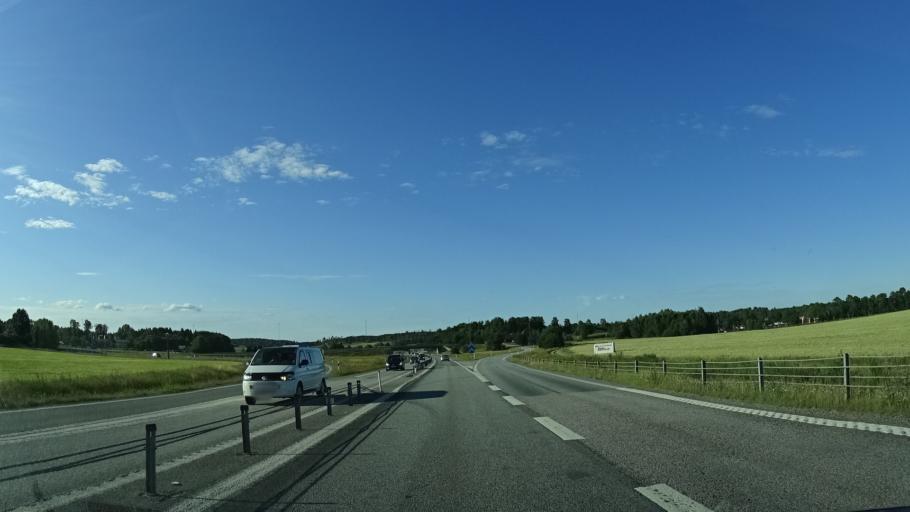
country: SE
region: Stockholm
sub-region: Osterakers Kommun
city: Akersberga
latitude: 59.5564
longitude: 18.2310
